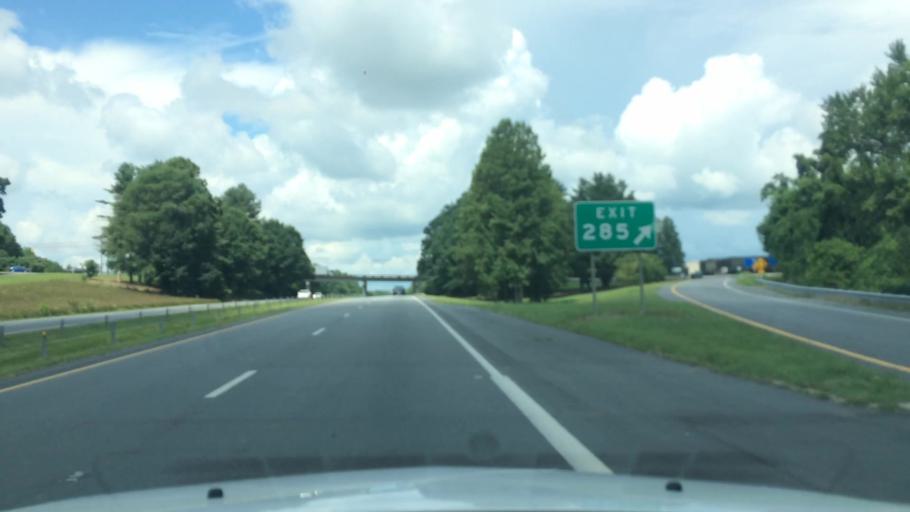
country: US
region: North Carolina
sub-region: Wilkes County
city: Wilkesboro
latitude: 36.1341
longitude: -81.1439
